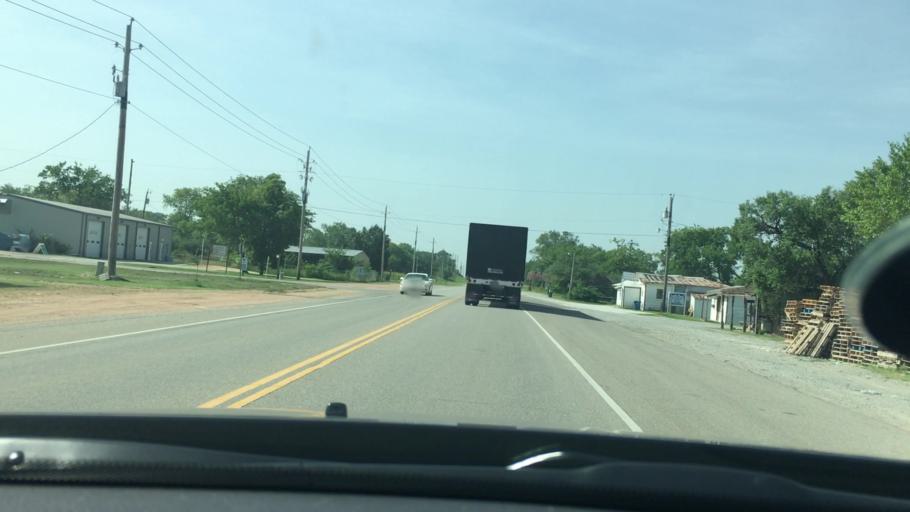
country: US
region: Oklahoma
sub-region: Coal County
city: Coalgate
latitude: 34.4717
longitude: -96.2177
